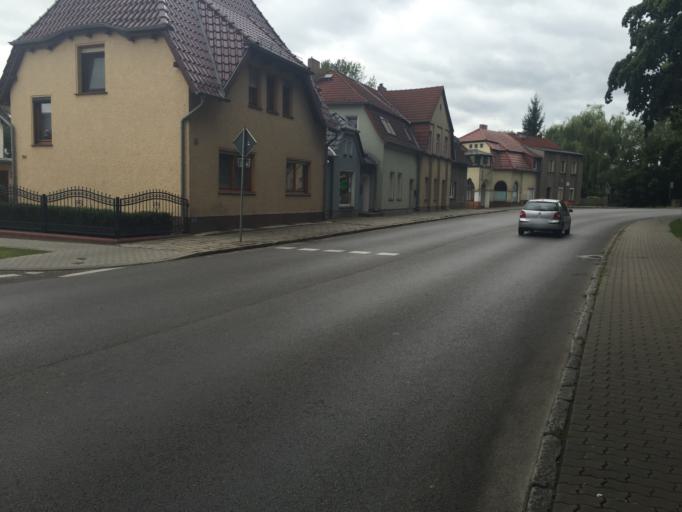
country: DE
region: Brandenburg
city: Luebben
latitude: 51.9411
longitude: 13.9071
